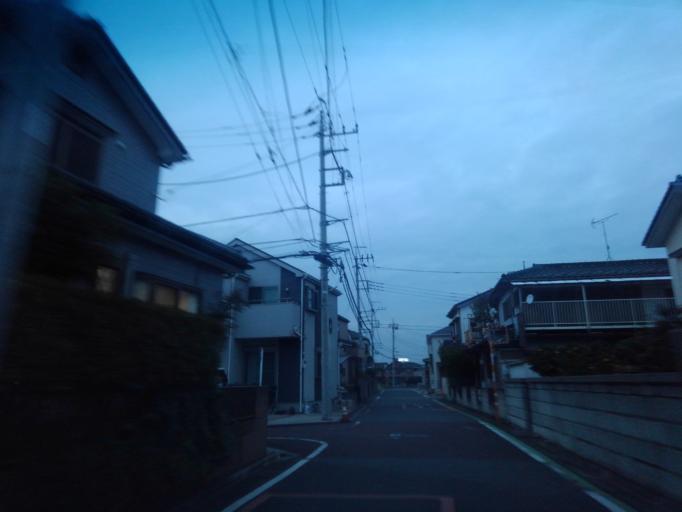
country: JP
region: Saitama
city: Tokorozawa
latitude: 35.8005
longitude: 139.4449
